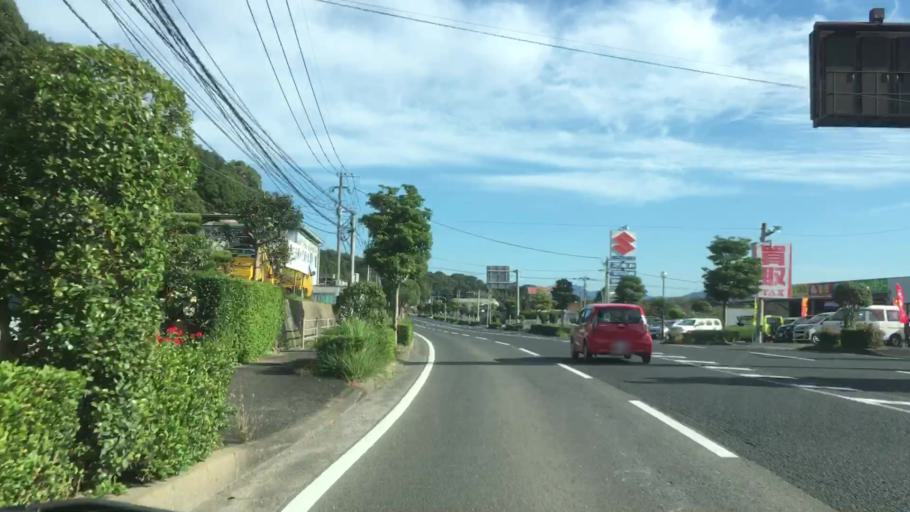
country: JP
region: Nagasaki
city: Sasebo
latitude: 33.1096
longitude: 129.7854
